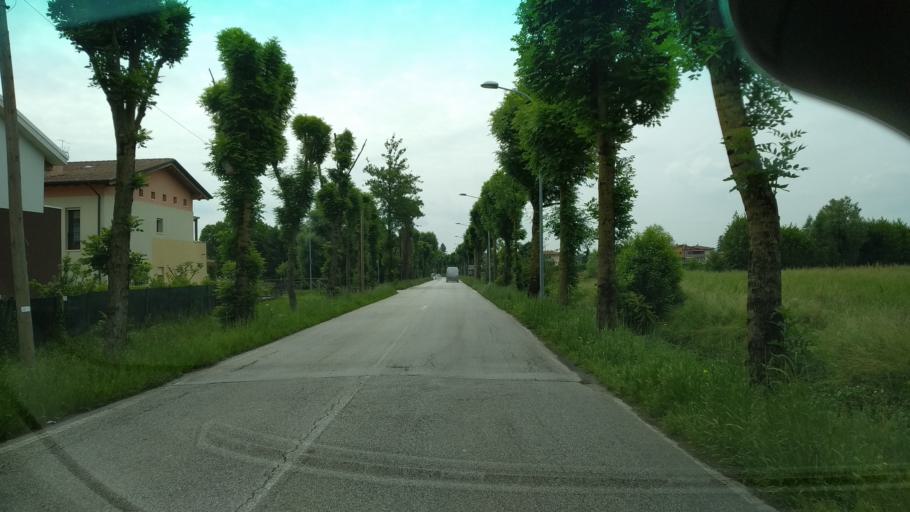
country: IT
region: Veneto
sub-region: Provincia di Vicenza
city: Caldogno-Rettorgole-Cresole
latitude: 45.5989
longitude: 11.5188
